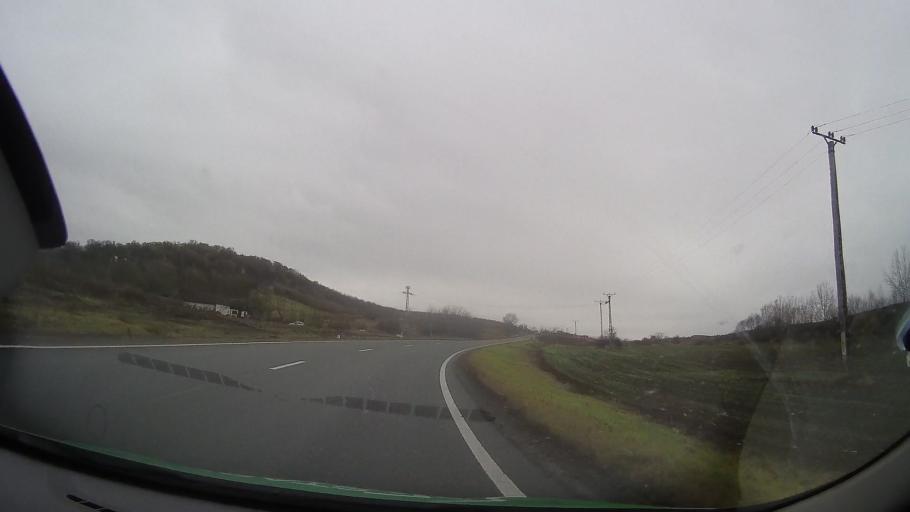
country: RO
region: Mures
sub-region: Comuna Breaza
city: Breaza
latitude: 46.7801
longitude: 24.6551
